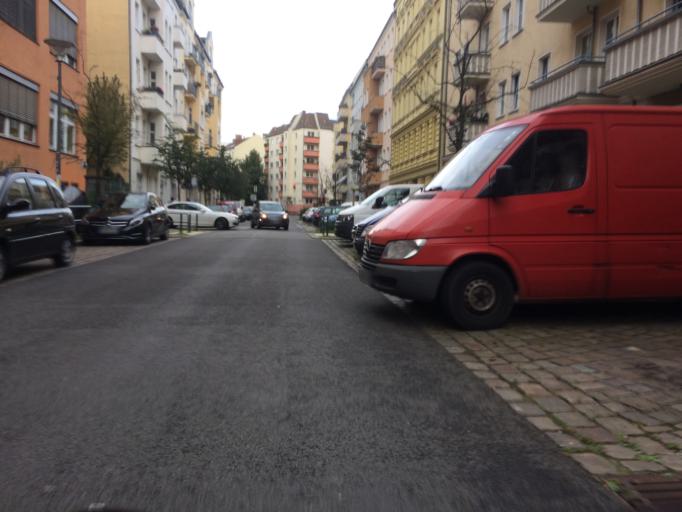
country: DE
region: Berlin
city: Friedrichshain Bezirk
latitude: 52.5112
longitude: 13.4719
